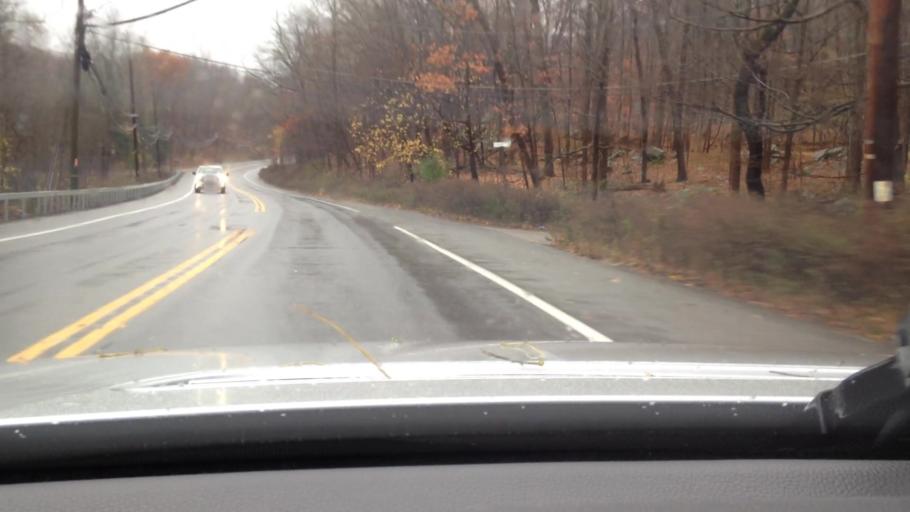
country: US
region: New York
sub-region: Westchester County
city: Peekskill
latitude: 41.3363
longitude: -73.9231
